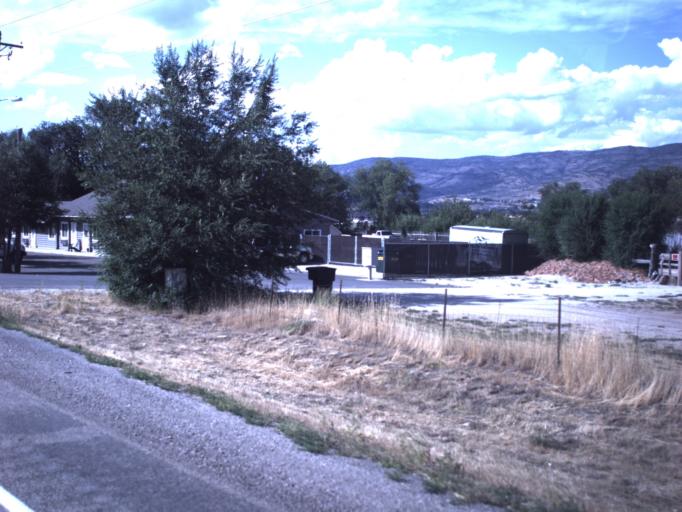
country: US
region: Utah
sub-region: Wasatch County
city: Heber
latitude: 40.4838
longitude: -111.4040
